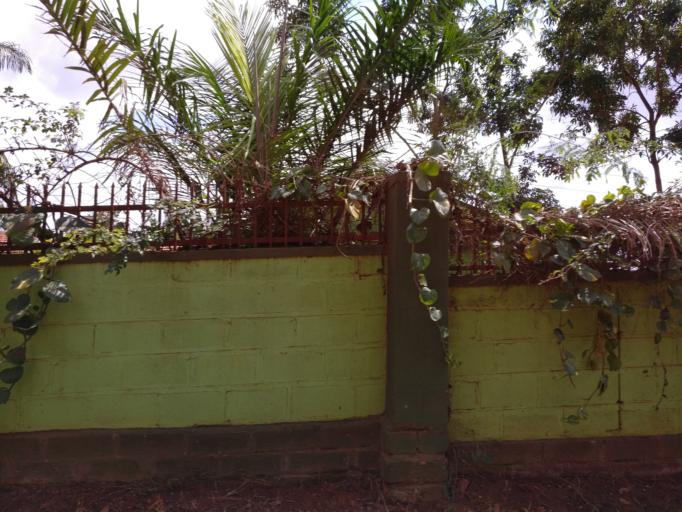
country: UG
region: Central Region
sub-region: Kampala District
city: Kampala
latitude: 0.2851
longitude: 32.5672
